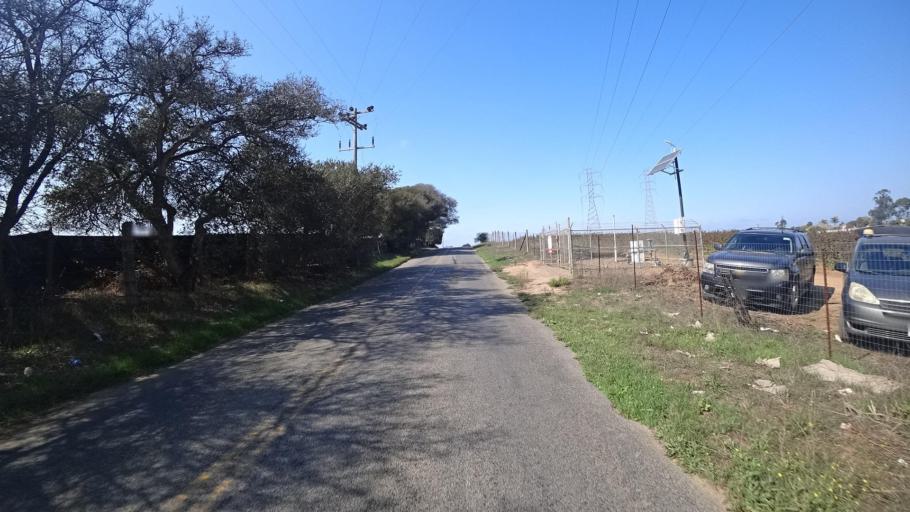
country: US
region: California
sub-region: Monterey County
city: Prunedale
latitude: 36.7896
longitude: -121.7055
